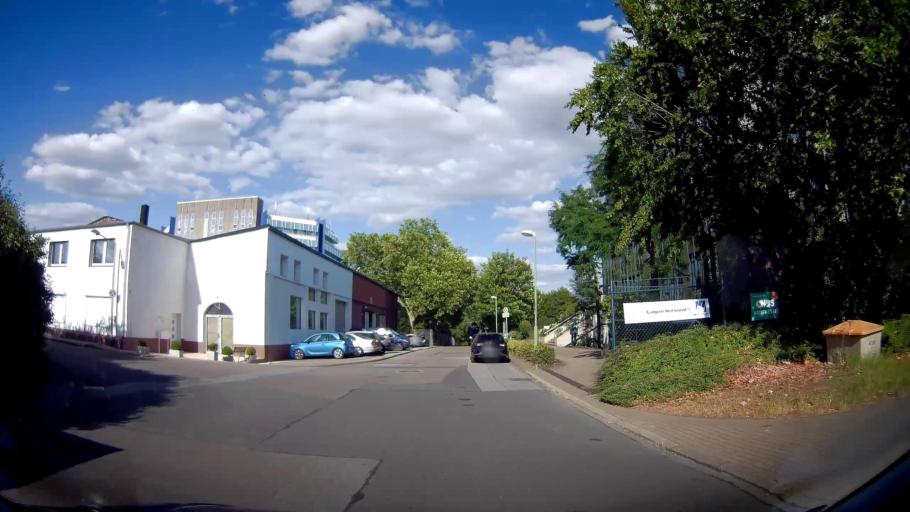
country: DE
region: North Rhine-Westphalia
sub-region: Regierungsbezirk Dusseldorf
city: Essen
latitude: 51.4679
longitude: 7.0038
